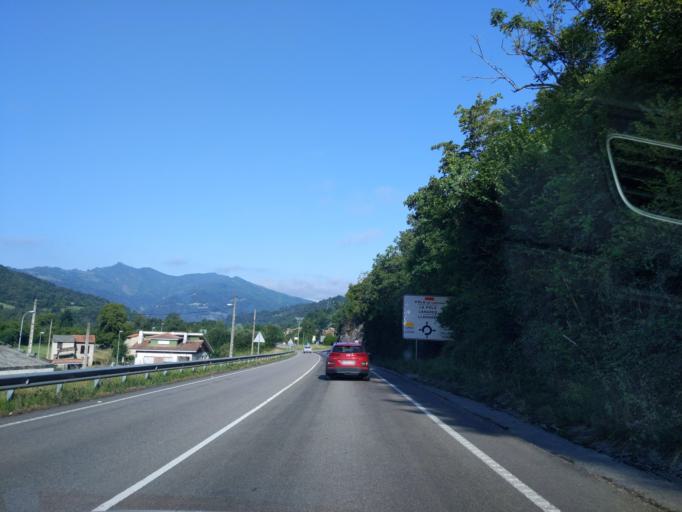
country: ES
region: Asturias
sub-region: Province of Asturias
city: Pola de Laviana
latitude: 43.2347
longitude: -5.5207
